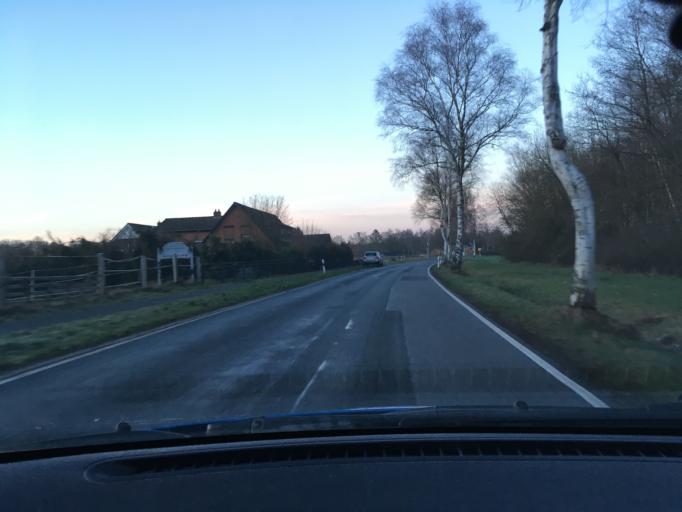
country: DE
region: Lower Saxony
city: Handeloh
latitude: 53.2583
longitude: 9.8821
